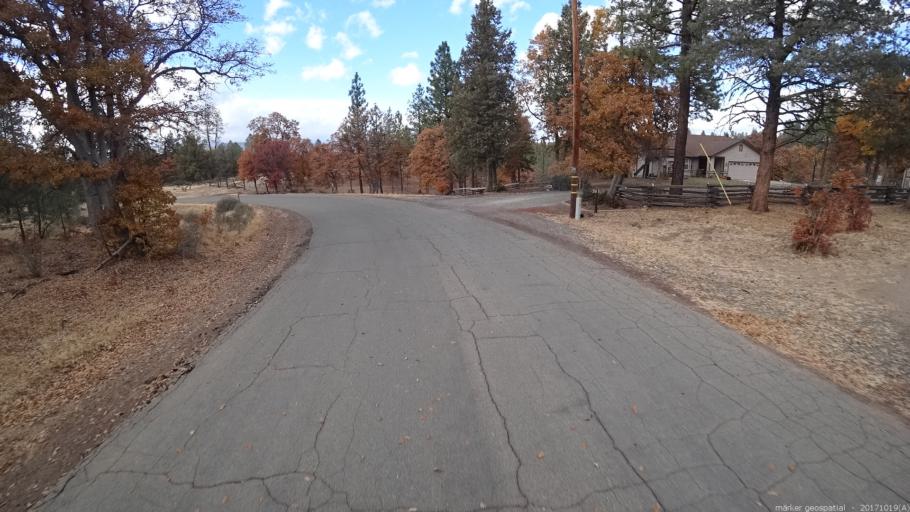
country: US
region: California
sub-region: Shasta County
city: Burney
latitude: 40.9756
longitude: -121.4410
